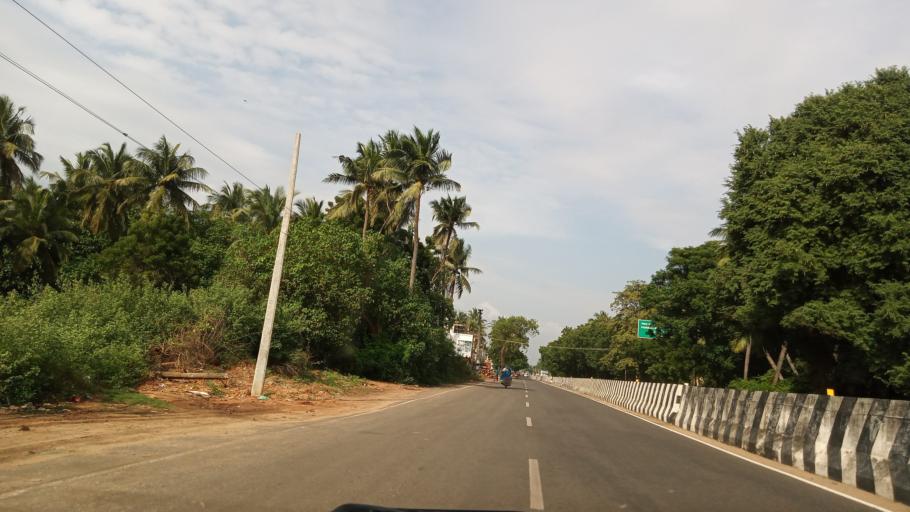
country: IN
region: Tamil Nadu
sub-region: Villupuram
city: Auroville
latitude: 12.0450
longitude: 79.8699
